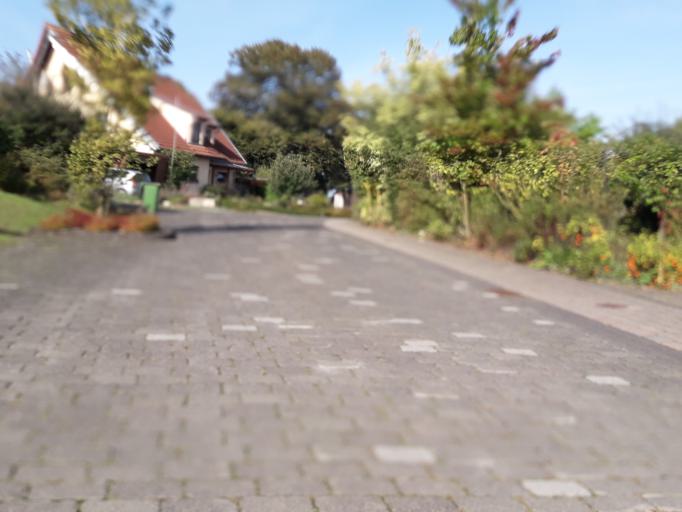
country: DE
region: North Rhine-Westphalia
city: Lichtenau
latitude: 51.6941
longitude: 8.8526
